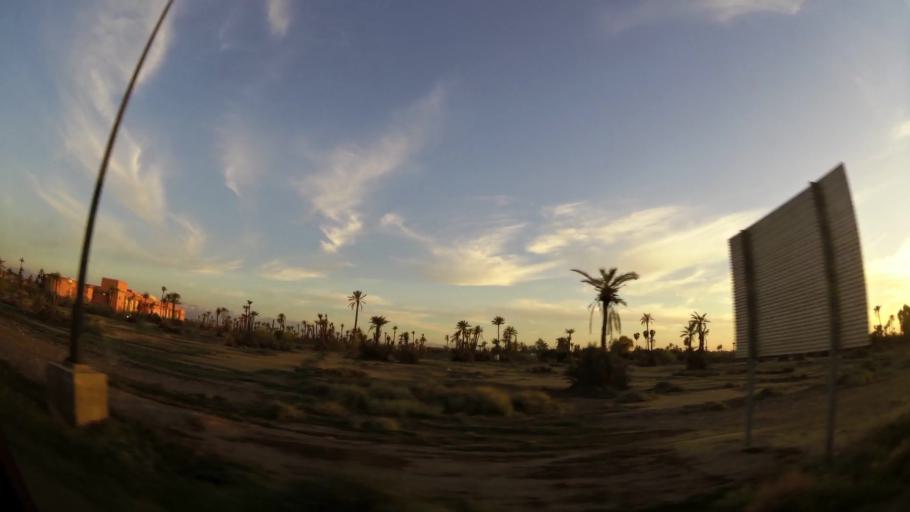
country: MA
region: Marrakech-Tensift-Al Haouz
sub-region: Marrakech
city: Marrakesh
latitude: 31.6874
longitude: -7.9959
